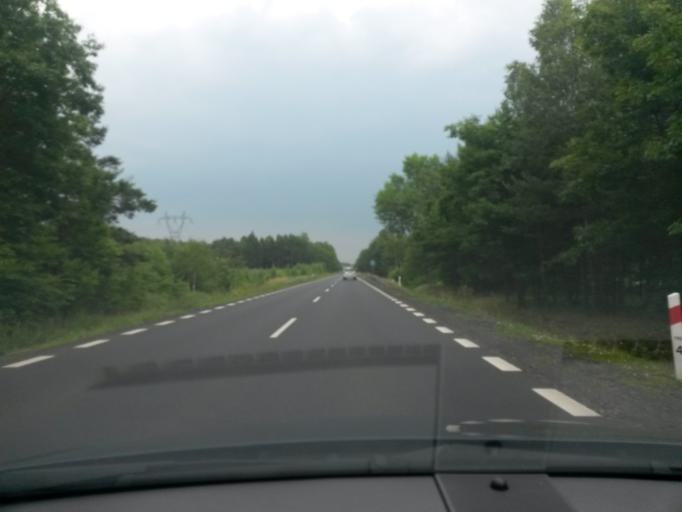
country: PL
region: Silesian Voivodeship
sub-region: Powiat czestochowski
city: Olsztyn
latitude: 50.7601
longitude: 19.2139
